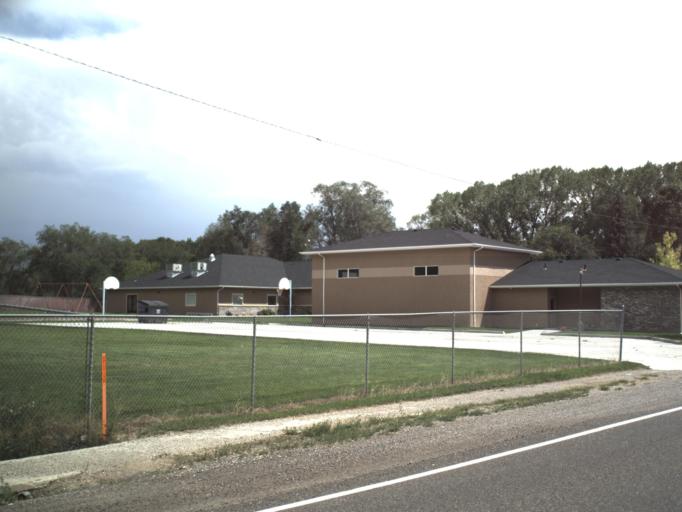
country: US
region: Utah
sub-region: Piute County
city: Junction
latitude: 38.1201
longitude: -112.0005
